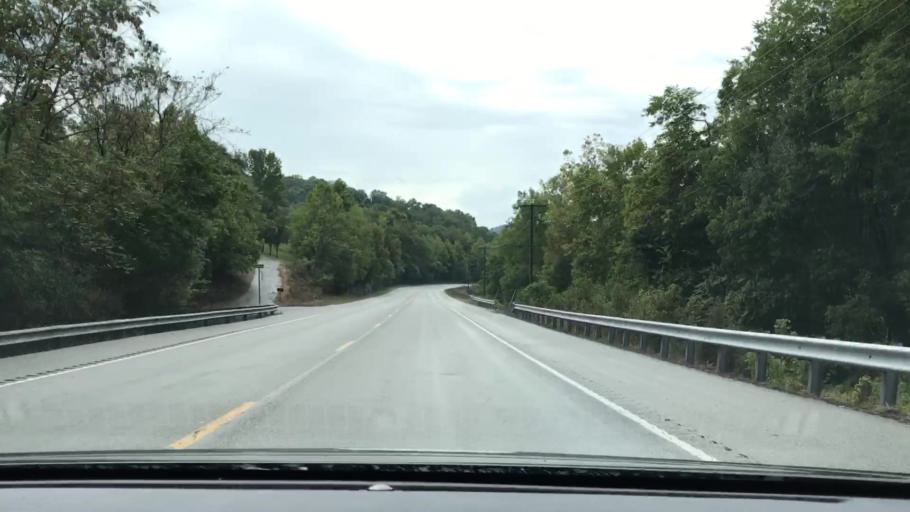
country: US
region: Tennessee
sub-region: Smith County
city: Carthage
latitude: 36.2935
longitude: -85.9840
